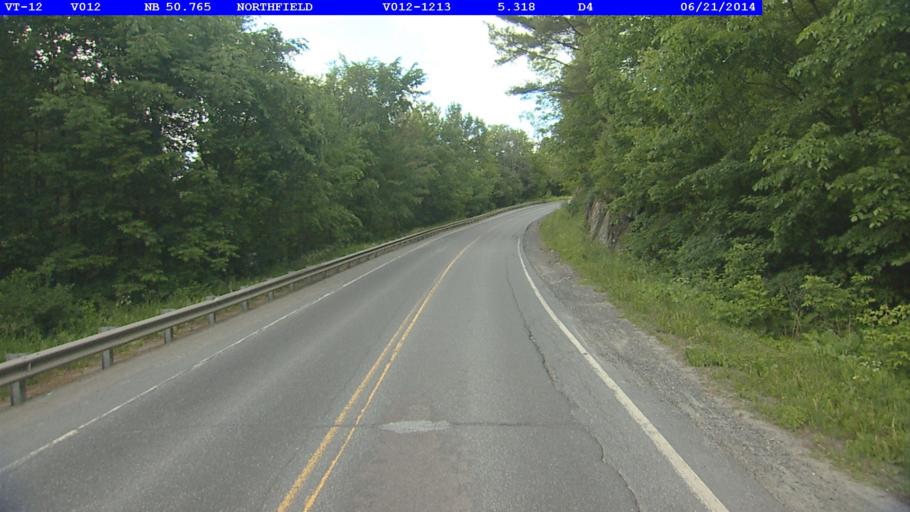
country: US
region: Vermont
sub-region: Washington County
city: Northfield
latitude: 44.1649
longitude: -72.6557
